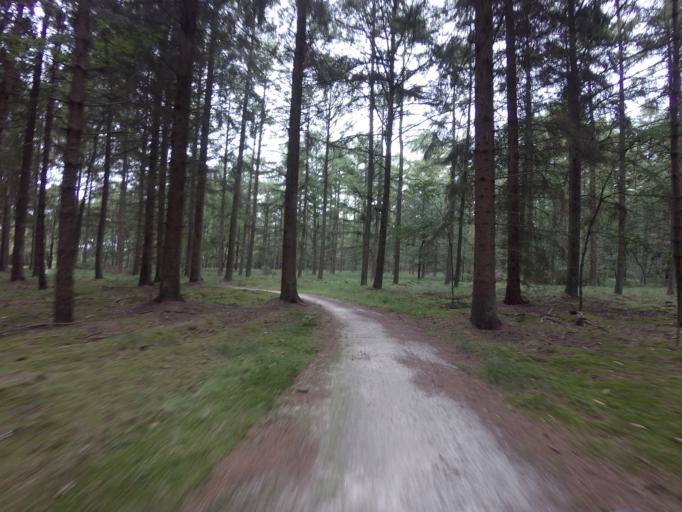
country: NL
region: Drenthe
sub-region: Gemeente Westerveld
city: Dwingeloo
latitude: 52.8911
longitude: 6.2942
